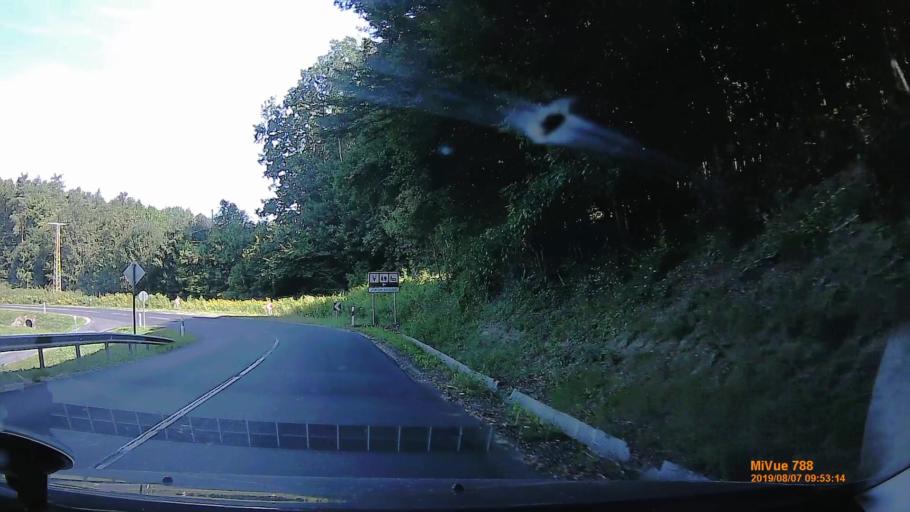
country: HU
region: Zala
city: Zalaegerszeg
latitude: 46.7334
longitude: 16.8848
